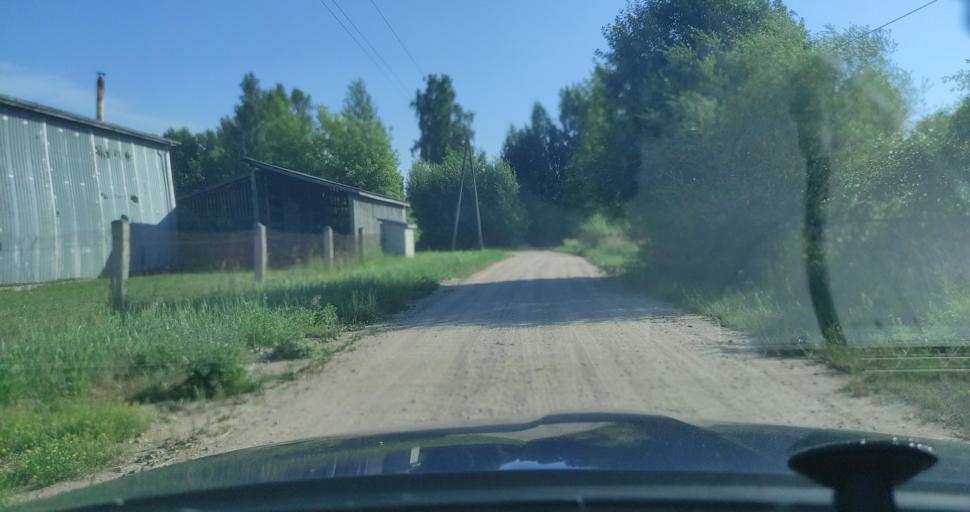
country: LV
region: Skrunda
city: Skrunda
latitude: 56.6834
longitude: 22.0051
